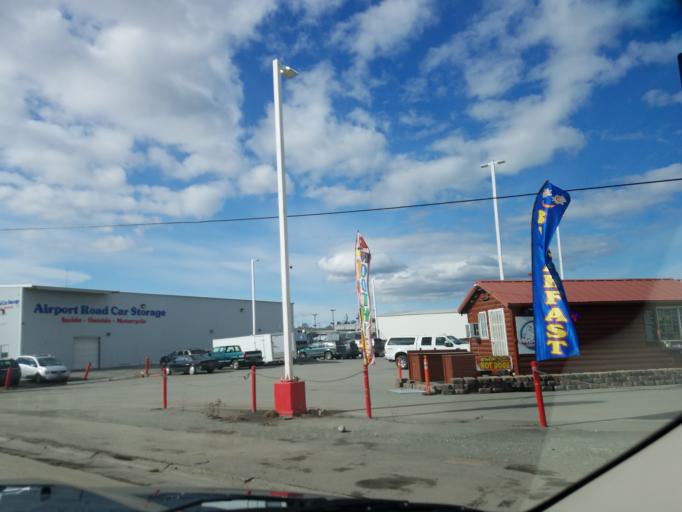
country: US
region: Alaska
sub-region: Anchorage Municipality
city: Anchorage
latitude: 61.1736
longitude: -149.8685
